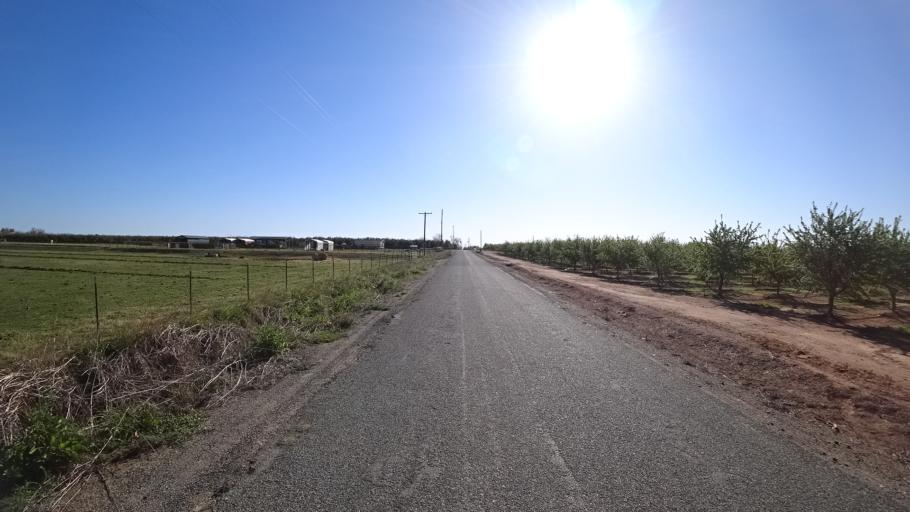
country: US
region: California
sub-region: Glenn County
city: Orland
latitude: 39.7262
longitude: -122.2435
